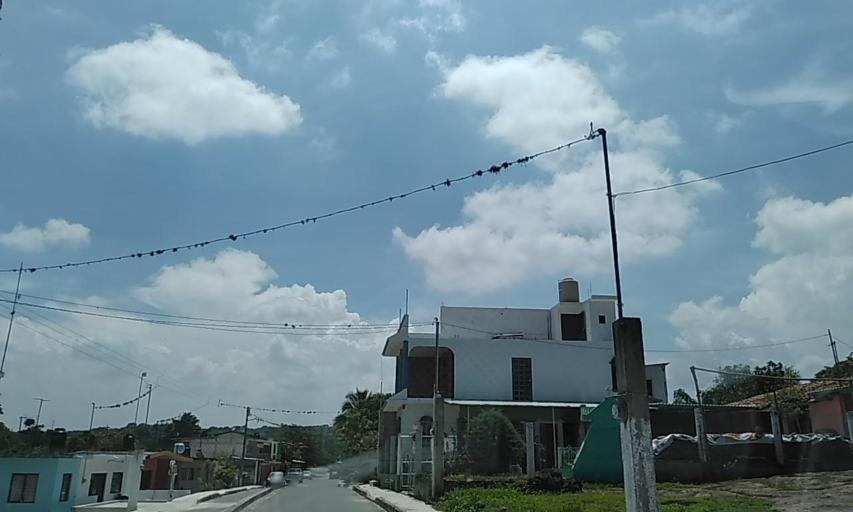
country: MX
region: Veracruz
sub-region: Emiliano Zapata
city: Dos Rios
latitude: 19.4399
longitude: -96.7551
